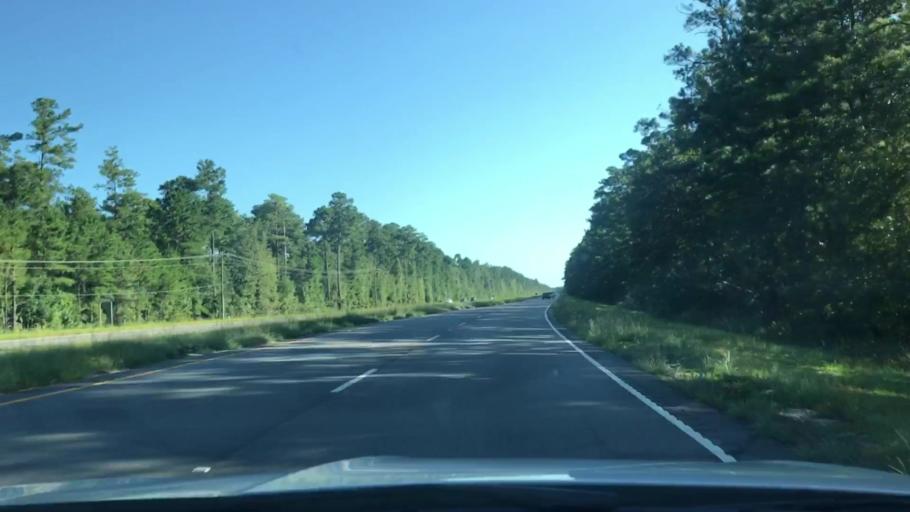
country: US
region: South Carolina
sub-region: Georgetown County
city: Georgetown
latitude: 33.2532
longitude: -79.3740
